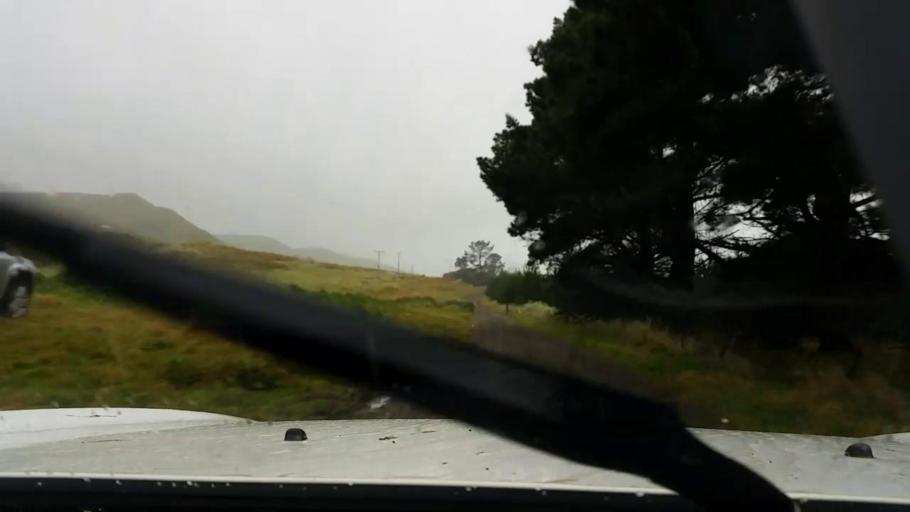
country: NZ
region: Wellington
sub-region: Masterton District
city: Masterton
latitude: -41.2533
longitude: 175.9124
